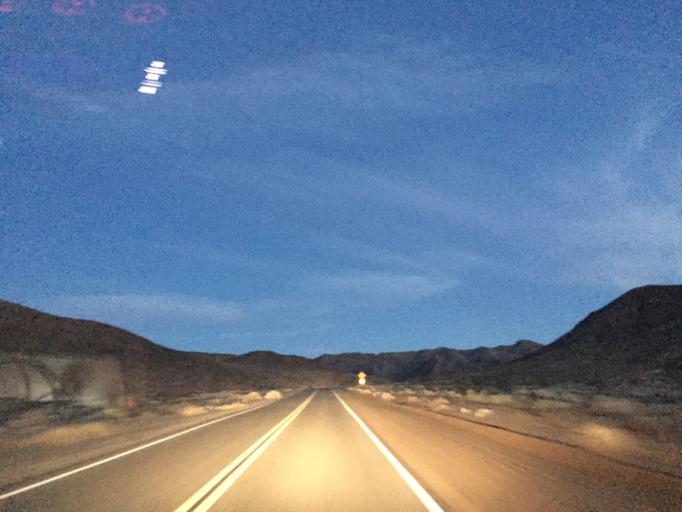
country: US
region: California
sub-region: San Bernardino County
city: Fort Irwin
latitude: 35.9117
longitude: -116.5837
